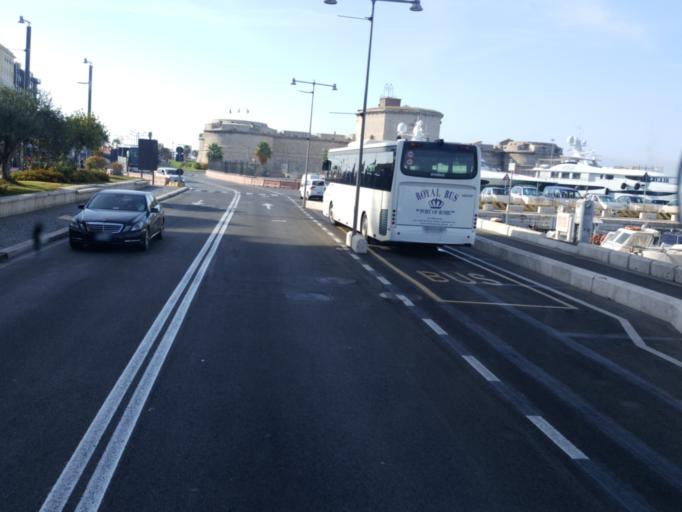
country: IT
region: Latium
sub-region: Citta metropolitana di Roma Capitale
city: Civitavecchia
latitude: 42.0928
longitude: 11.7902
